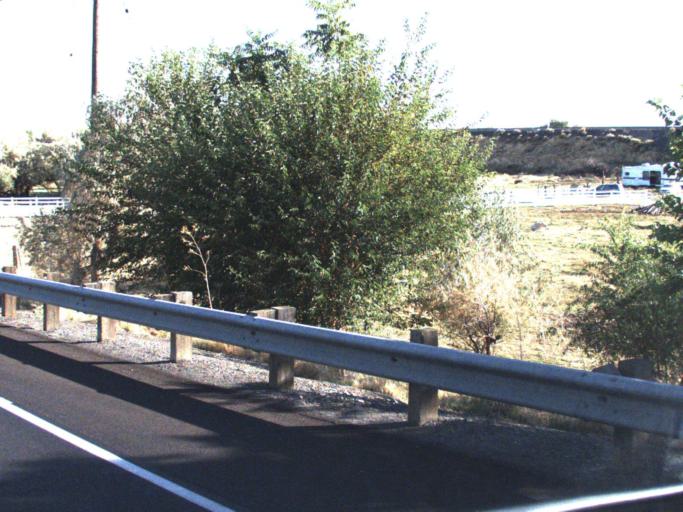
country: US
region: Washington
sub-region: Franklin County
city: Pasco
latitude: 46.1980
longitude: -119.0879
